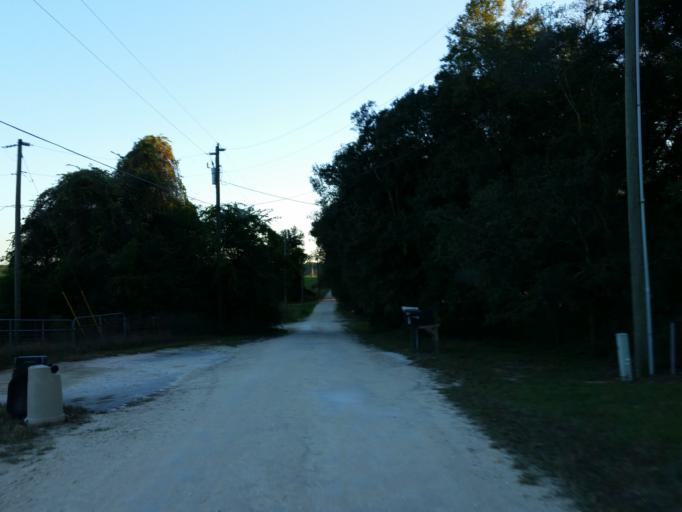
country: US
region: Florida
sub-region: Hernando County
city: Hill 'n Dale
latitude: 28.5272
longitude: -82.2508
